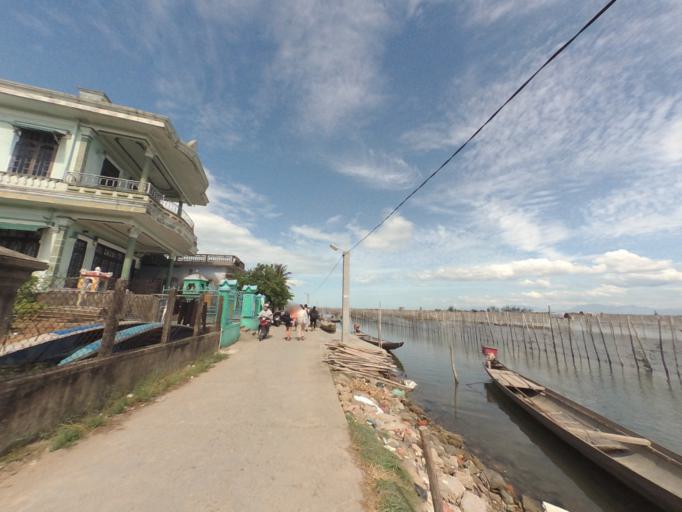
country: VN
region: Thua Thien-Hue
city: Hue
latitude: 16.5375
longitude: 107.6379
